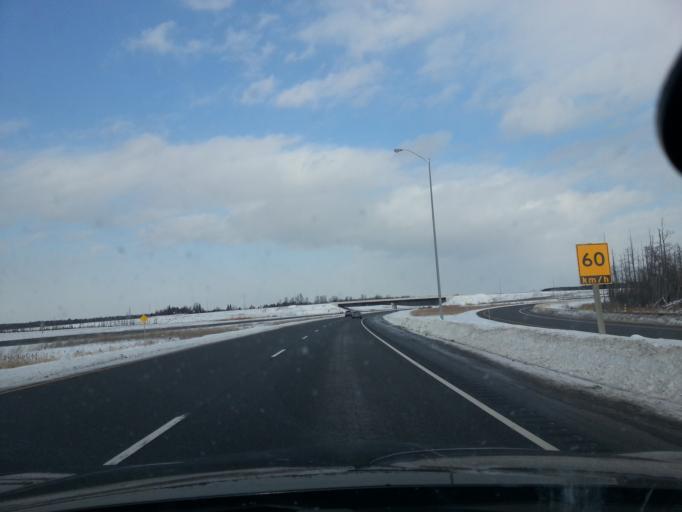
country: CA
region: Ontario
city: Carleton Place
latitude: 45.1997
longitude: -76.0428
